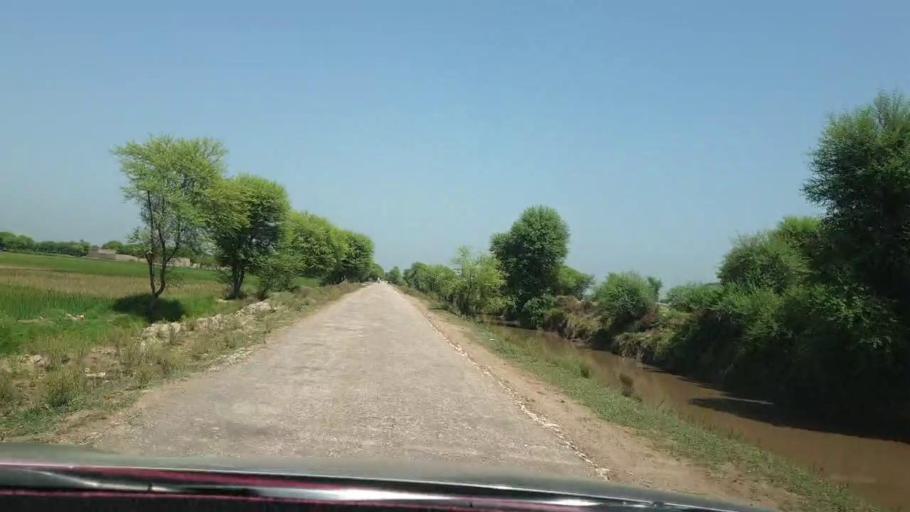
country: PK
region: Sindh
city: Warah
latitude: 27.5185
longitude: 67.8124
